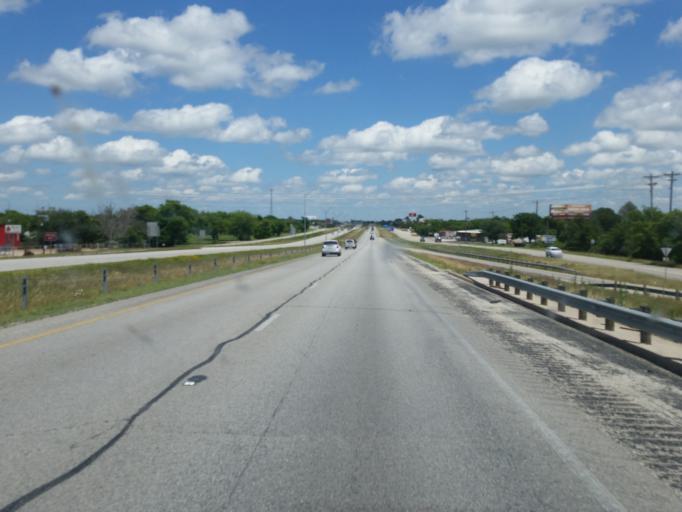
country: US
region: Texas
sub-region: Callahan County
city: Clyde
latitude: 32.4147
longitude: -99.5058
